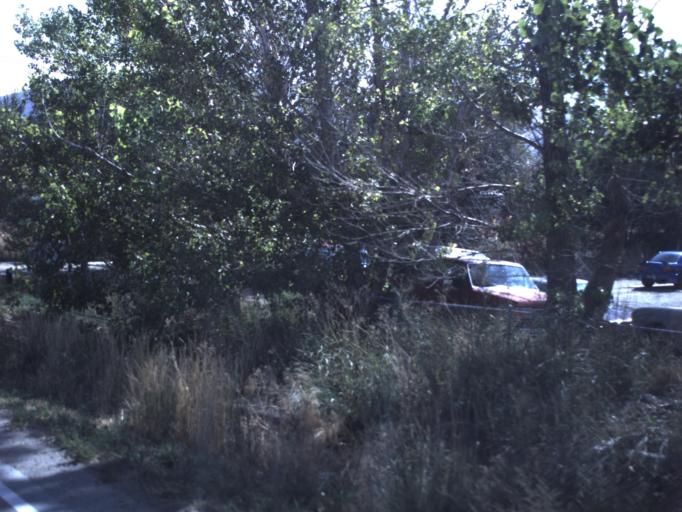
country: US
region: Utah
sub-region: Salt Lake County
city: Bluffdale
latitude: 40.4861
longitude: -111.9162
